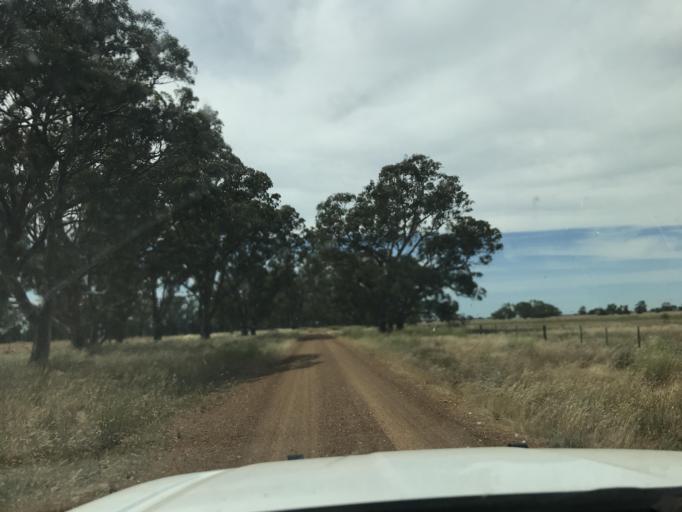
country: AU
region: South Australia
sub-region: Wattle Range
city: Penola
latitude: -37.0176
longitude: 141.4804
